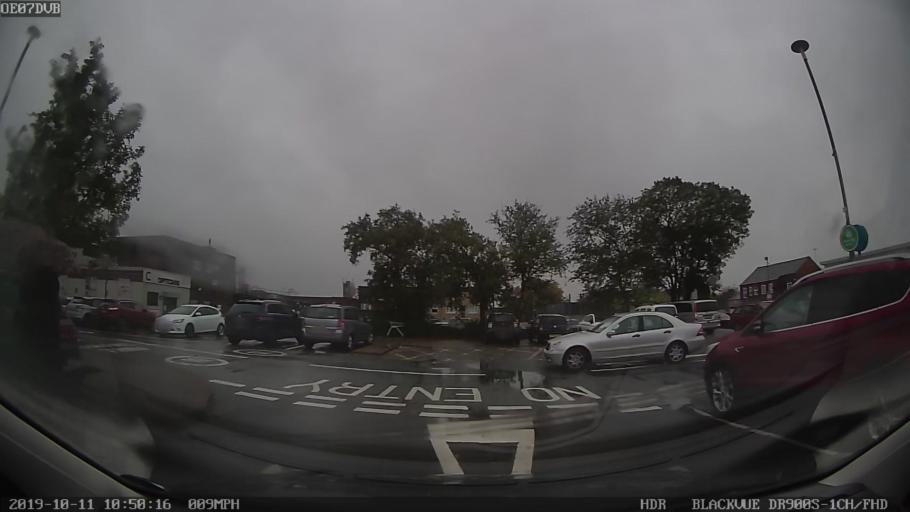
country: GB
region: England
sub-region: Borough of Oldham
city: Oldham
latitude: 53.5481
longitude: -2.1405
